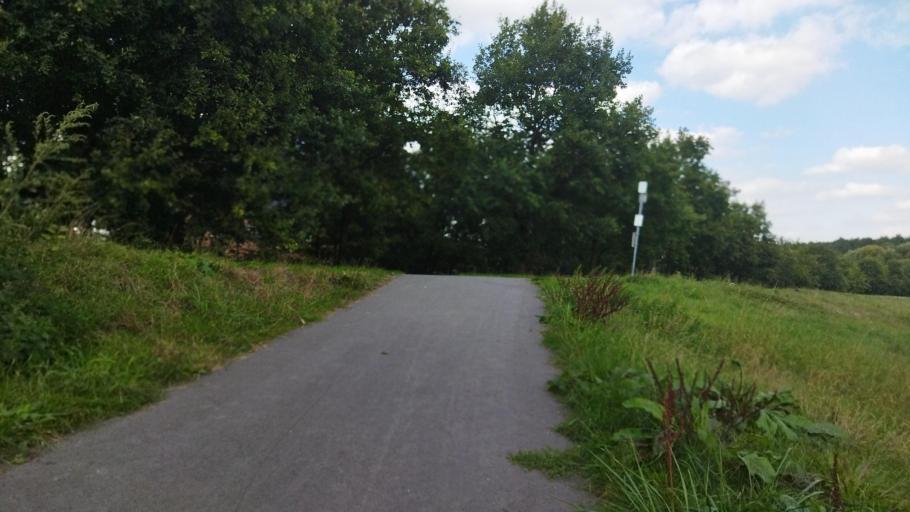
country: DE
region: Lower Saxony
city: Haren
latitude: 52.7906
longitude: 7.2585
